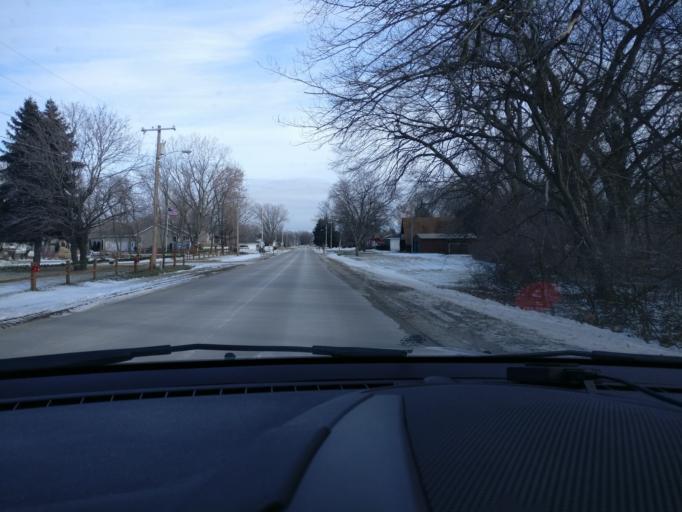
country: US
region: Nebraska
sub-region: Dodge County
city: Fremont
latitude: 41.4142
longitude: -96.5067
